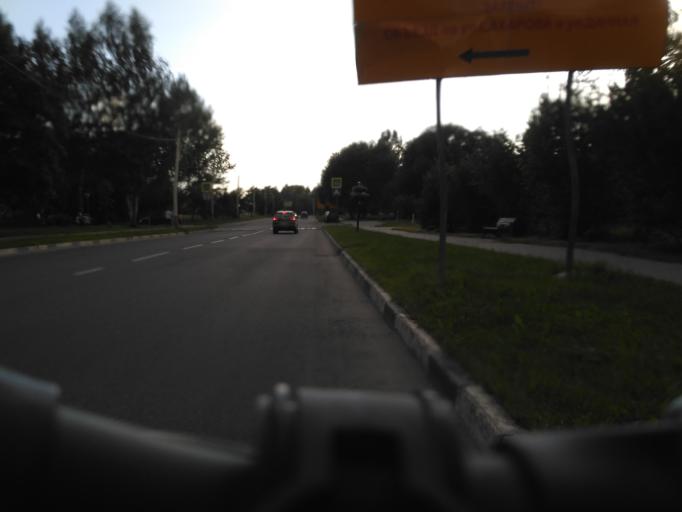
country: RU
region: Moskovskaya
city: Dubna
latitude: 56.7449
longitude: 37.1745
